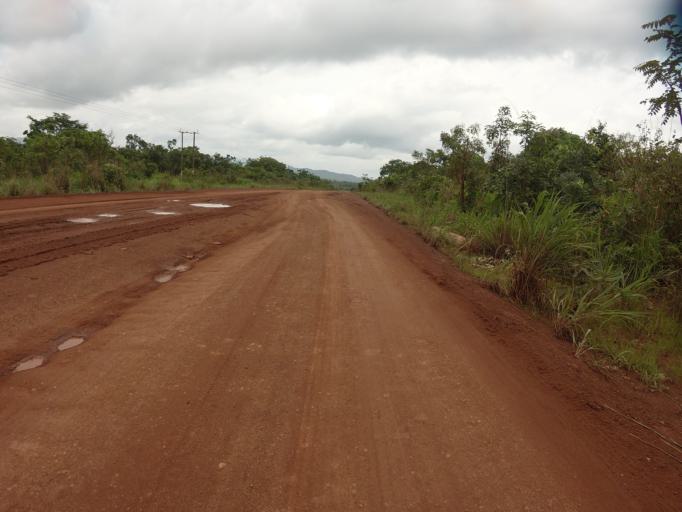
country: GH
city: Kpandae
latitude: 8.3045
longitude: 0.4852
